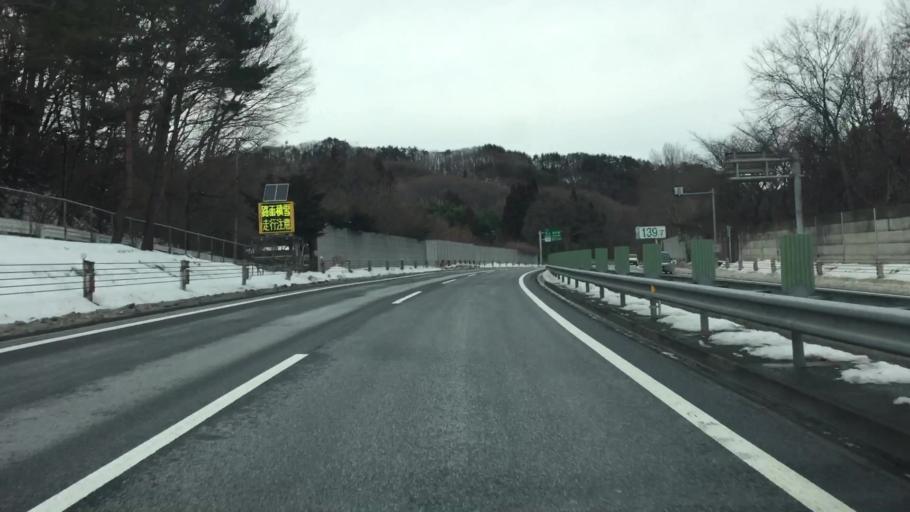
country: JP
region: Gunma
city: Numata
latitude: 36.7344
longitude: 138.9750
